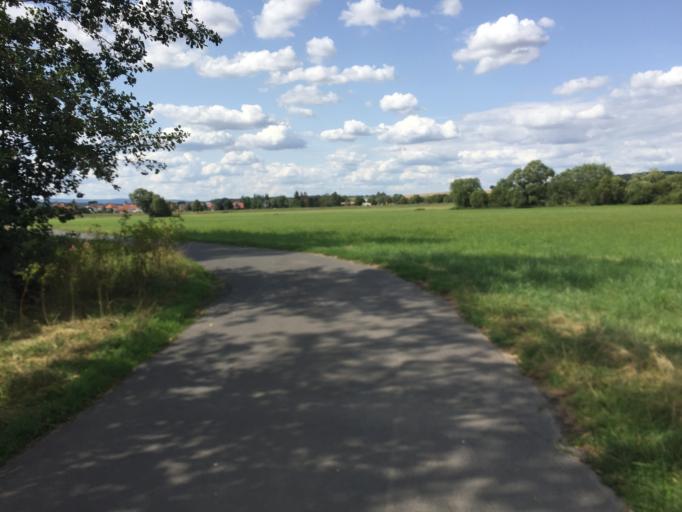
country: DE
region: Hesse
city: Schwalmstadt
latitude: 50.9071
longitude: 9.2518
